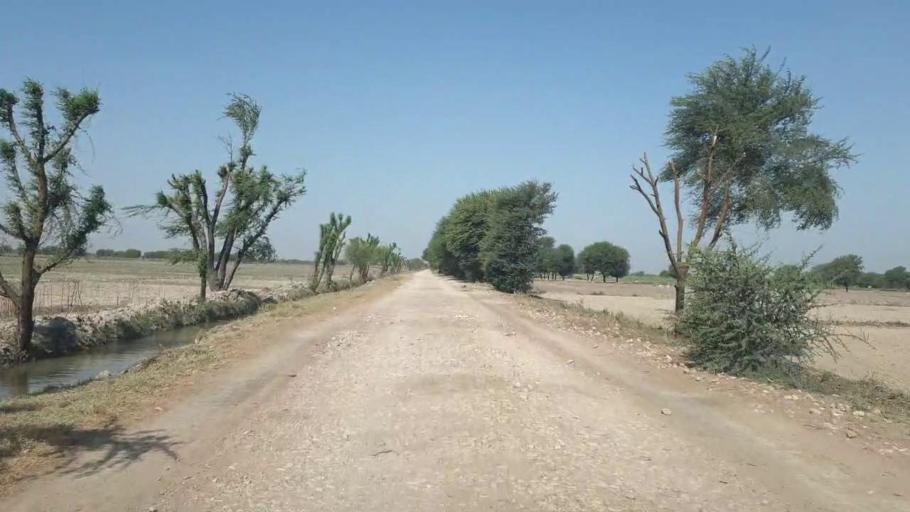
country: PK
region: Sindh
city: Umarkot
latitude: 25.2900
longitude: 69.6383
